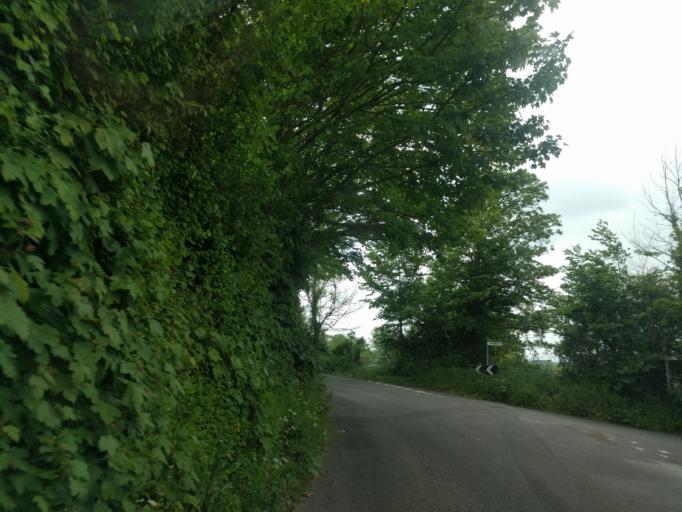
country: GB
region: England
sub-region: Somerset
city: Langport
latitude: 51.0496
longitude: -2.8100
